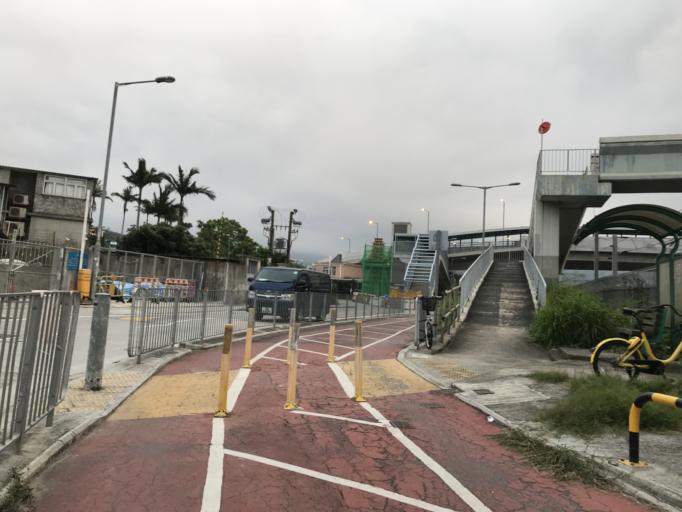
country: HK
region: Tai Po
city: Tai Po
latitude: 22.4759
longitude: 114.1546
